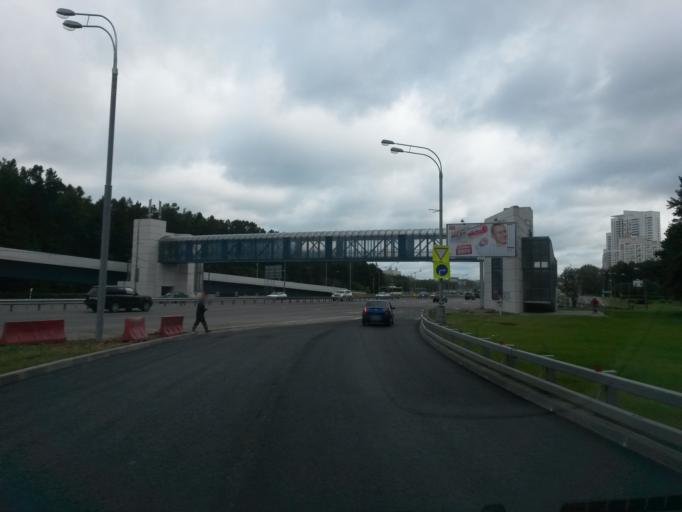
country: RU
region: Moskovskaya
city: Mosrentgen
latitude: 55.6400
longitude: 37.4631
